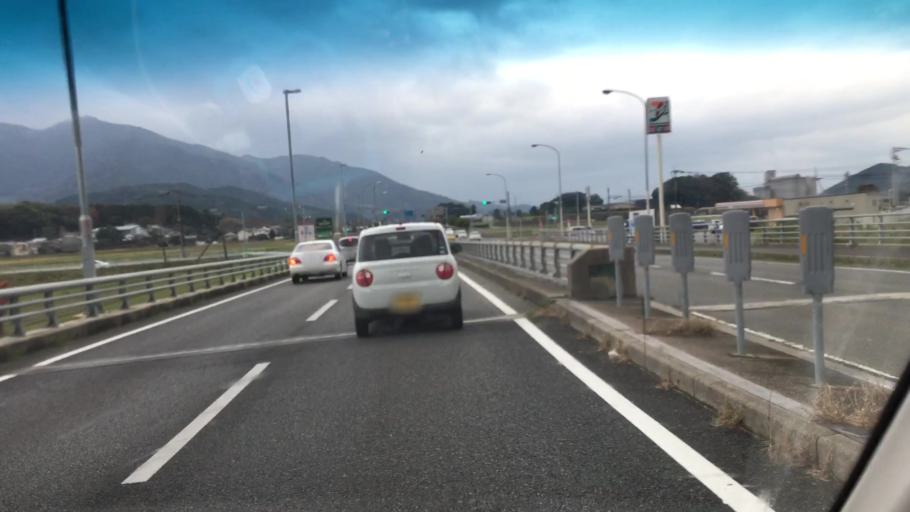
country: JP
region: Fukuoka
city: Maebaru-chuo
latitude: 33.5227
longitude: 130.1685
